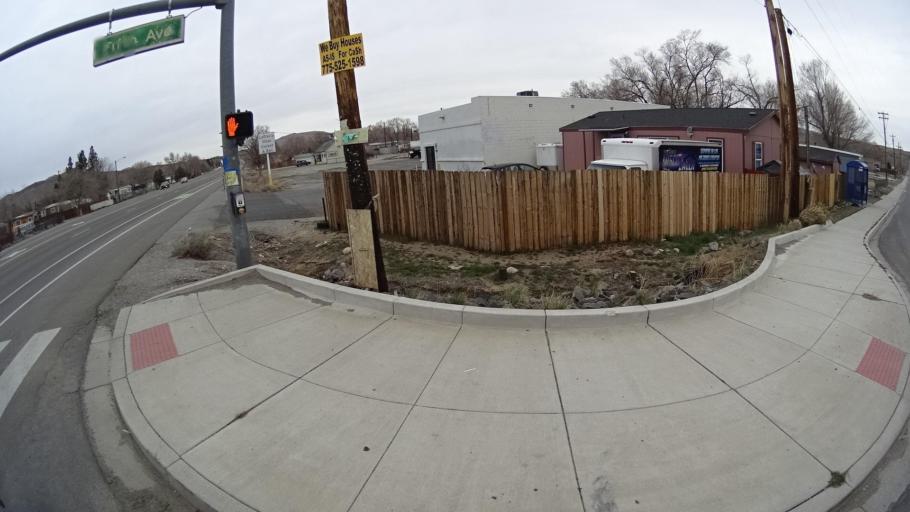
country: US
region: Nevada
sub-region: Washoe County
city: Sun Valley
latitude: 39.5927
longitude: -119.7805
